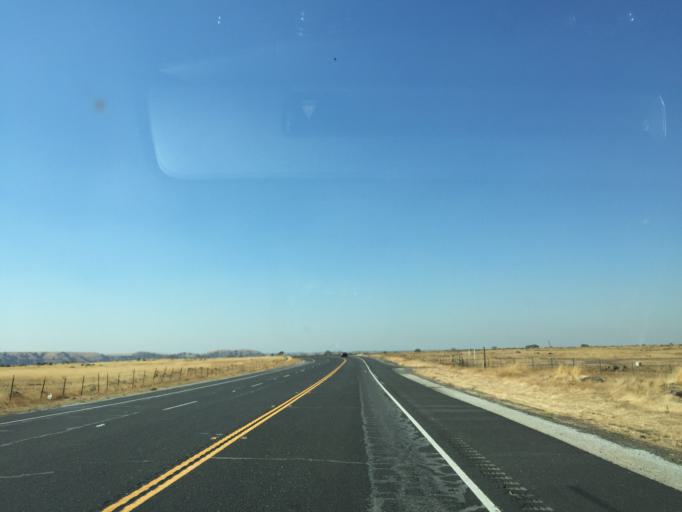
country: US
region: California
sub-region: Calaveras County
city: Copperopolis
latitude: 37.8213
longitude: -120.6462
